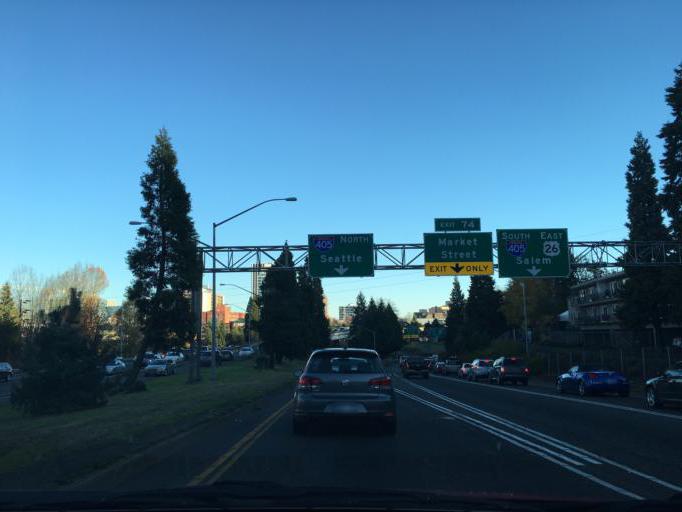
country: US
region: Oregon
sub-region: Multnomah County
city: Portland
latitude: 45.5153
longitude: -122.6931
